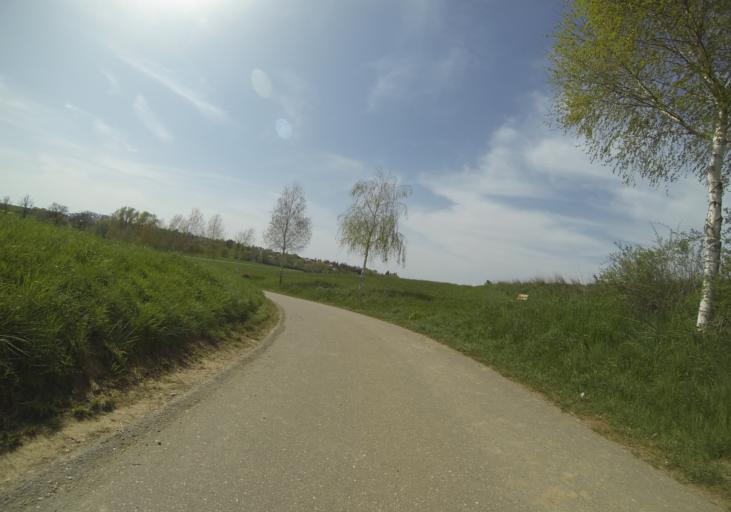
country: DE
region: Baden-Wuerttemberg
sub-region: Tuebingen Region
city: Burgrieden
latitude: 48.2474
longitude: 9.9188
